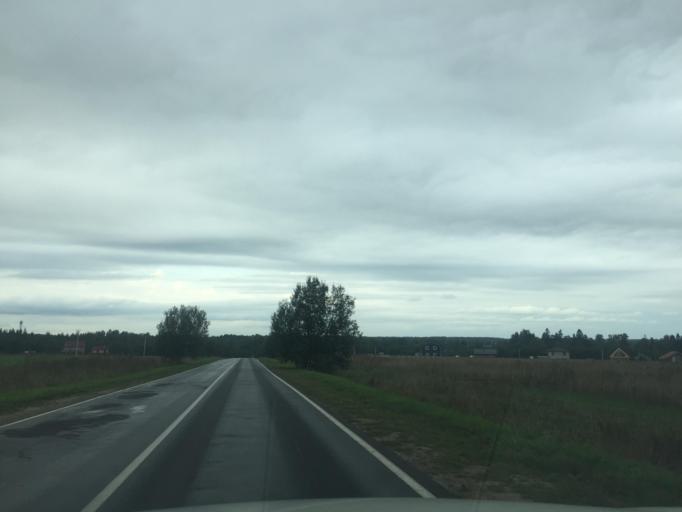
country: RU
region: Leningrad
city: Siverskiy
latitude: 59.3356
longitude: 30.0297
